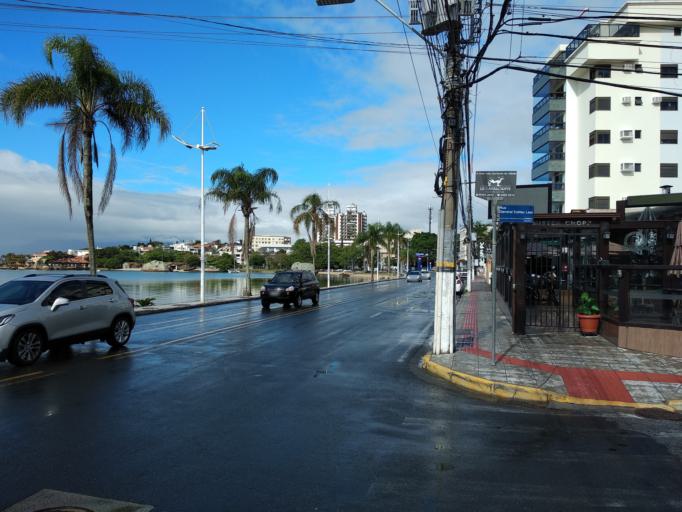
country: BR
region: Santa Catarina
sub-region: Sao Jose
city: Campinas
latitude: -27.6127
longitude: -48.5844
